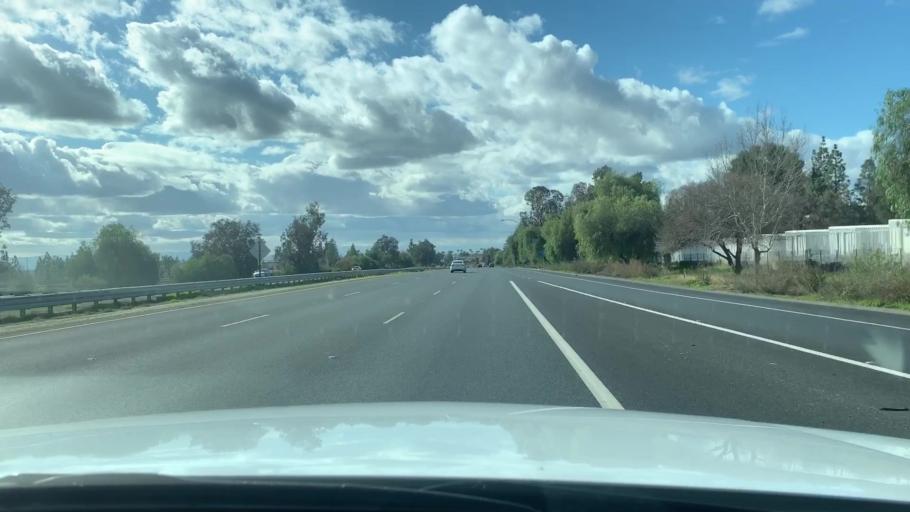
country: US
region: California
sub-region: Kern County
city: Bakersfield
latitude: 35.3965
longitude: -118.9532
